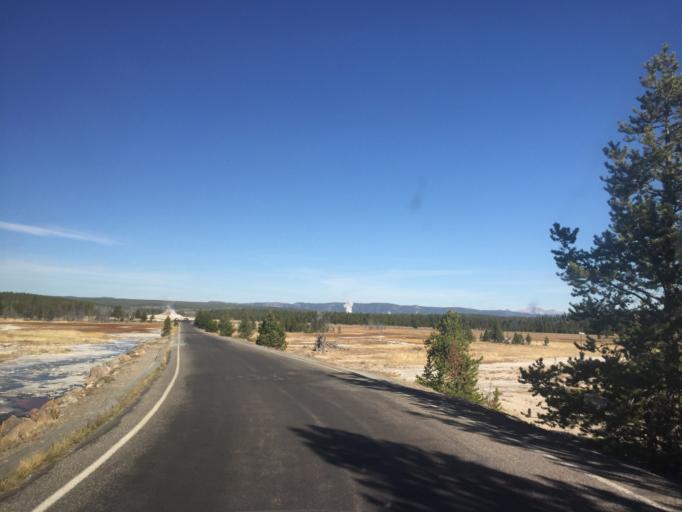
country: US
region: Montana
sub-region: Gallatin County
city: West Yellowstone
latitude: 44.5367
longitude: -110.7995
